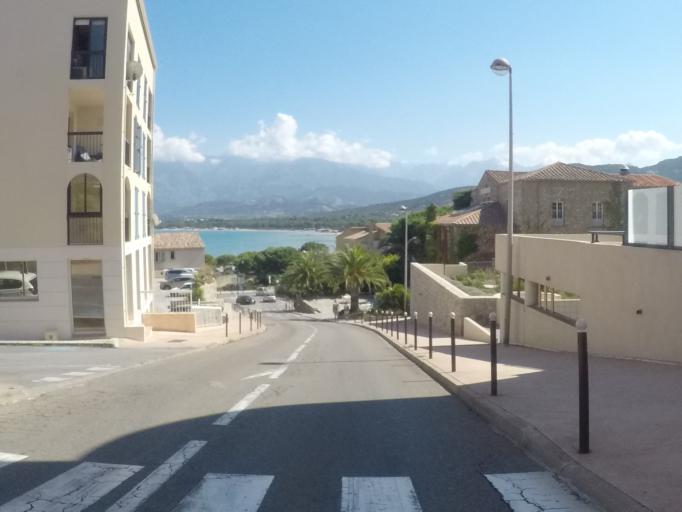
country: FR
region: Corsica
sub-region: Departement de la Haute-Corse
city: Calvi
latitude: 42.5643
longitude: 8.7537
